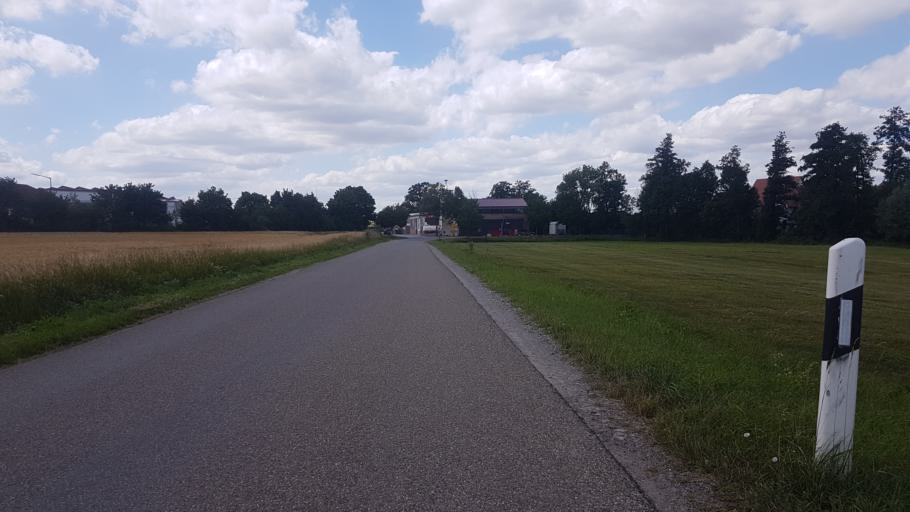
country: DE
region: Bavaria
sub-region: Regierungsbezirk Mittelfranken
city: Geslau
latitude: 49.3635
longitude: 10.3114
